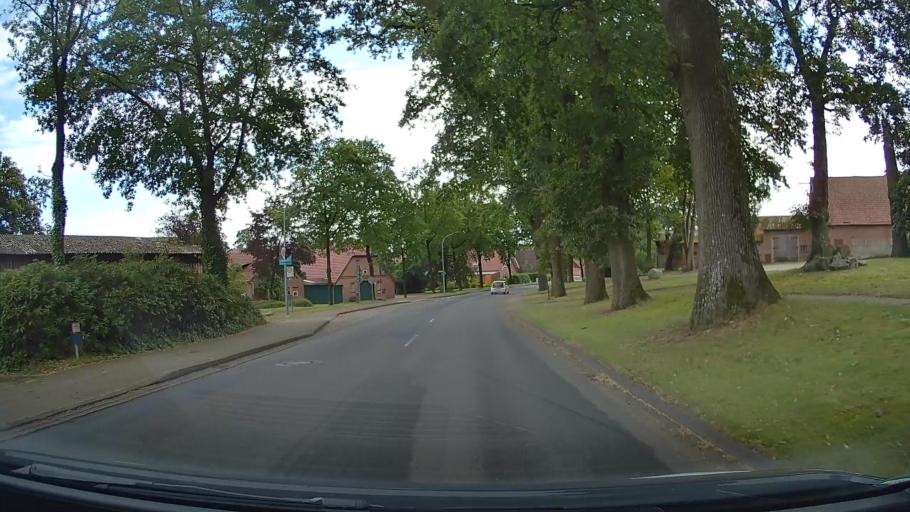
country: DE
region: Lower Saxony
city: Rhade
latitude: 53.3122
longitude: 9.1378
